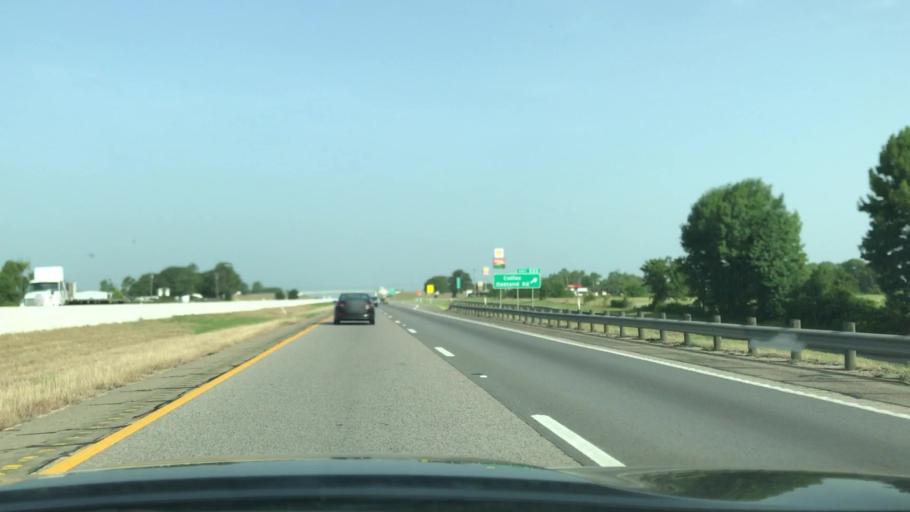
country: US
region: Texas
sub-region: Van Zandt County
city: Canton
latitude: 32.5404
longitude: -95.7512
